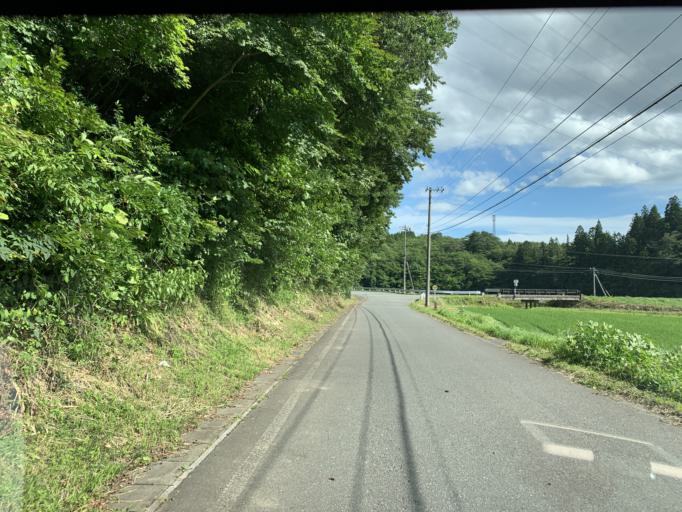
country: JP
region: Iwate
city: Ichinoseki
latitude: 38.9363
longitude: 141.0098
